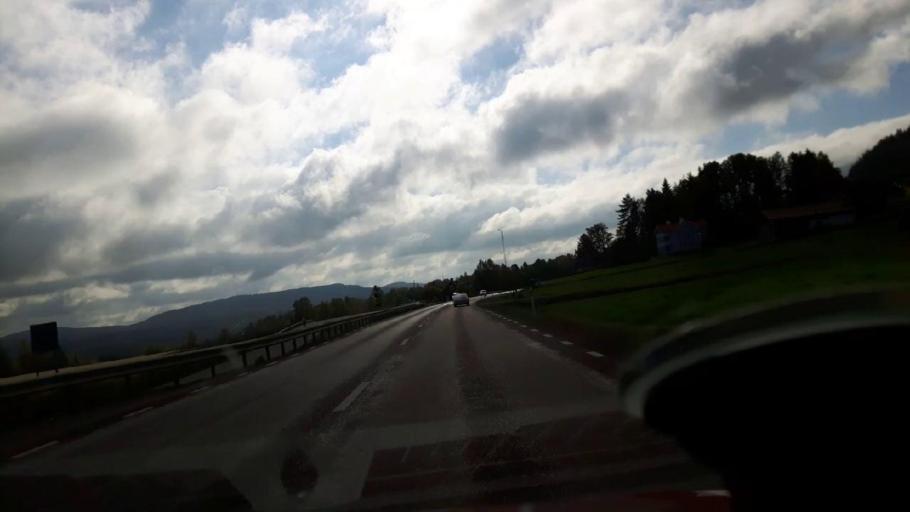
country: SE
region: Gaevleborg
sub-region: Ljusdals Kommun
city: Jaervsoe
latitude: 61.7283
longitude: 16.1672
